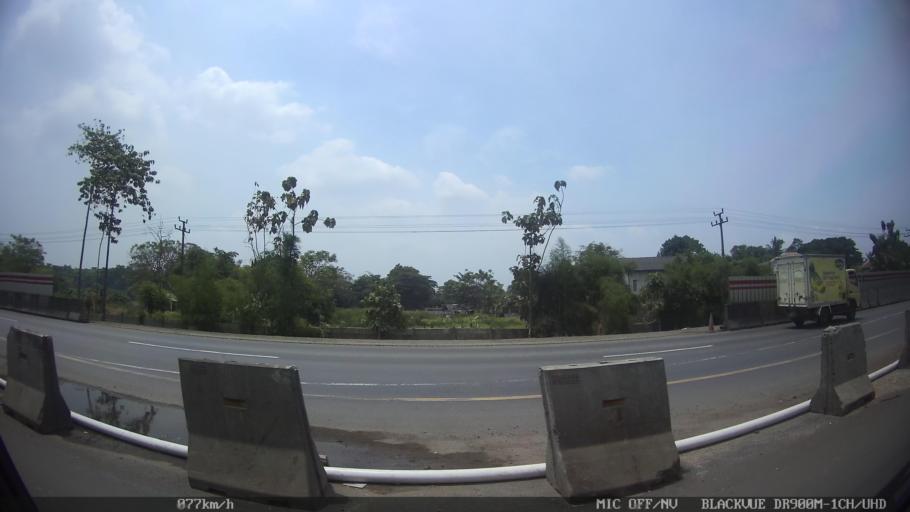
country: ID
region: West Java
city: Kresek
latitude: -6.1500
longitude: 106.3058
